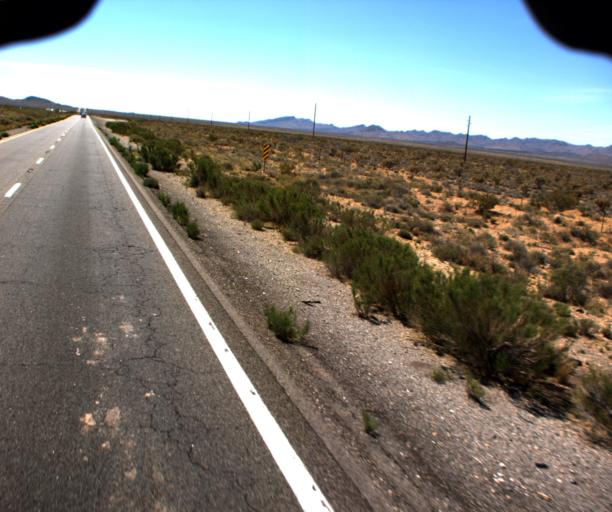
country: US
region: Arizona
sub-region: Mohave County
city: Dolan Springs
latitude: 35.4797
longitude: -114.3182
